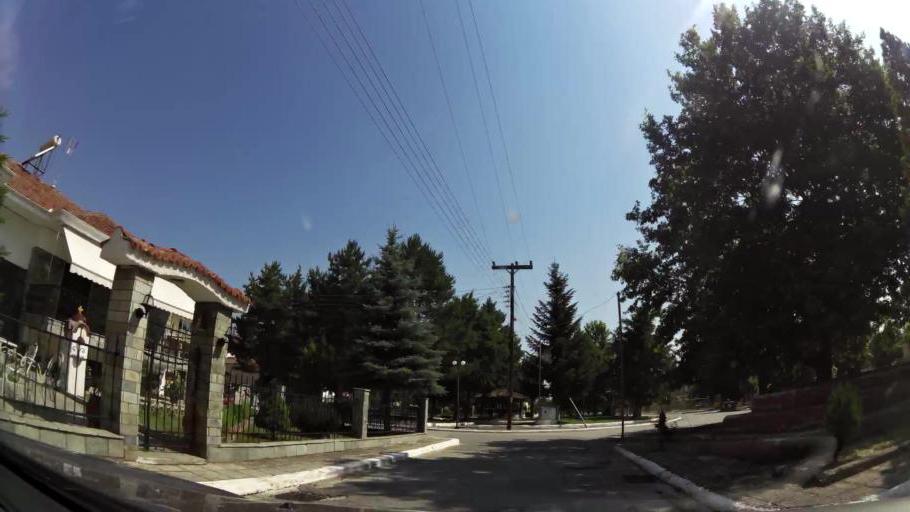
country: GR
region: West Macedonia
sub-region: Nomos Kozanis
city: Koila
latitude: 40.3369
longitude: 21.7859
